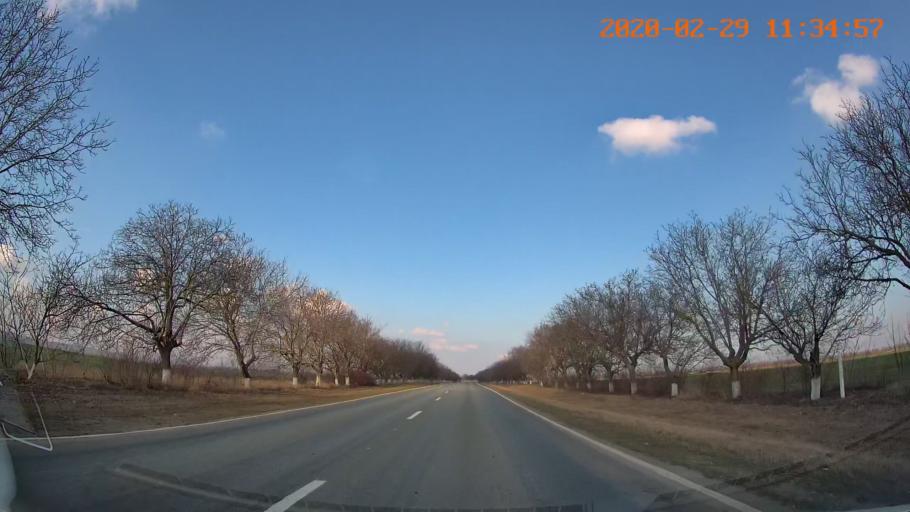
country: MD
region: Rezina
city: Saharna
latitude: 47.5730
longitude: 29.0683
